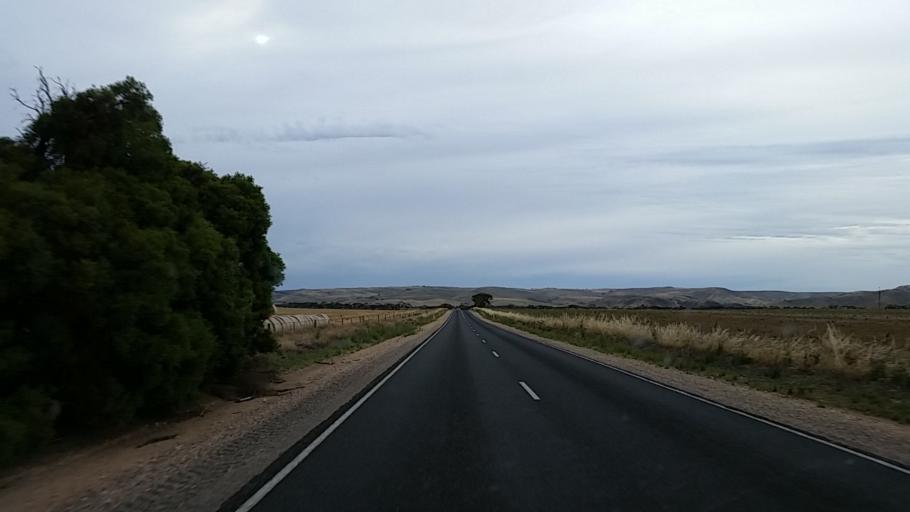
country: AU
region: South Australia
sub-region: Mid Murray
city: Mannum
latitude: -34.7555
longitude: 139.2552
